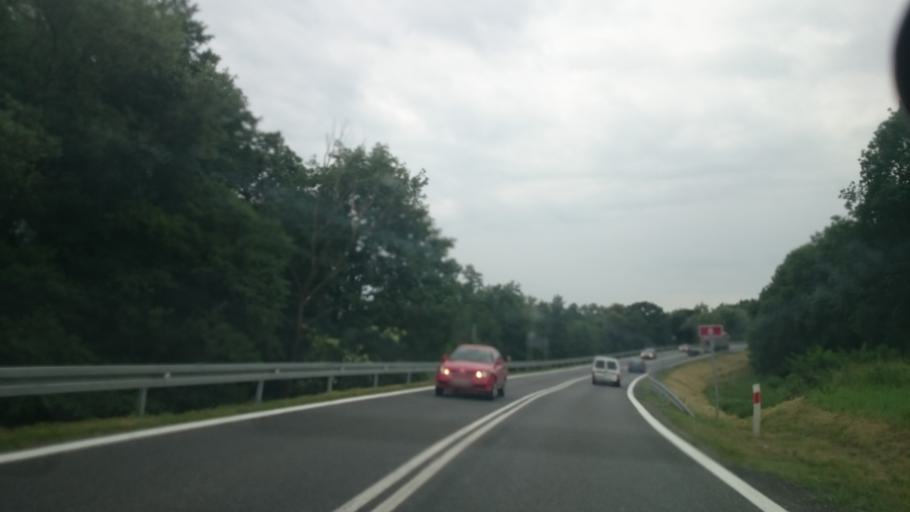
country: PL
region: Lower Silesian Voivodeship
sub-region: Powiat dzierzoniowski
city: Niemcza
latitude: 50.7347
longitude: 16.8375
